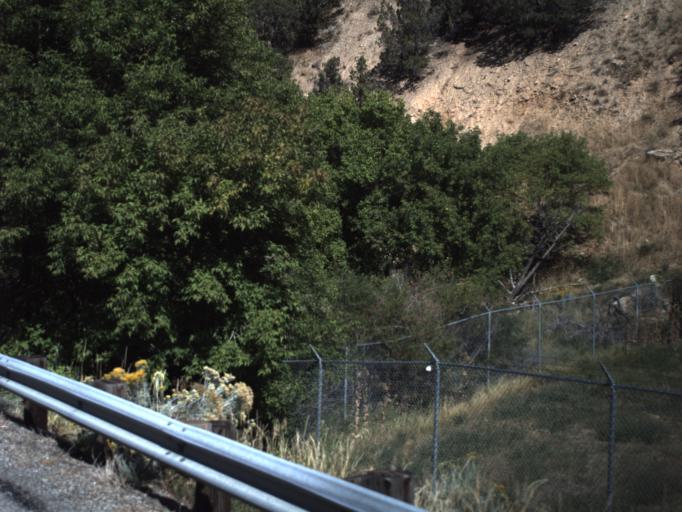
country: US
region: Utah
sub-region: Cache County
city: Millville
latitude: 41.6238
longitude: -111.7346
